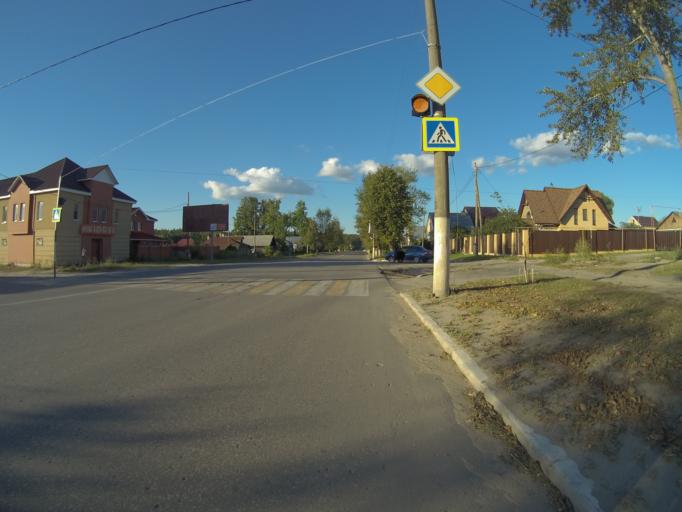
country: RU
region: Vladimir
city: Gus'-Khrustal'nyy
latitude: 55.6232
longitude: 40.6817
